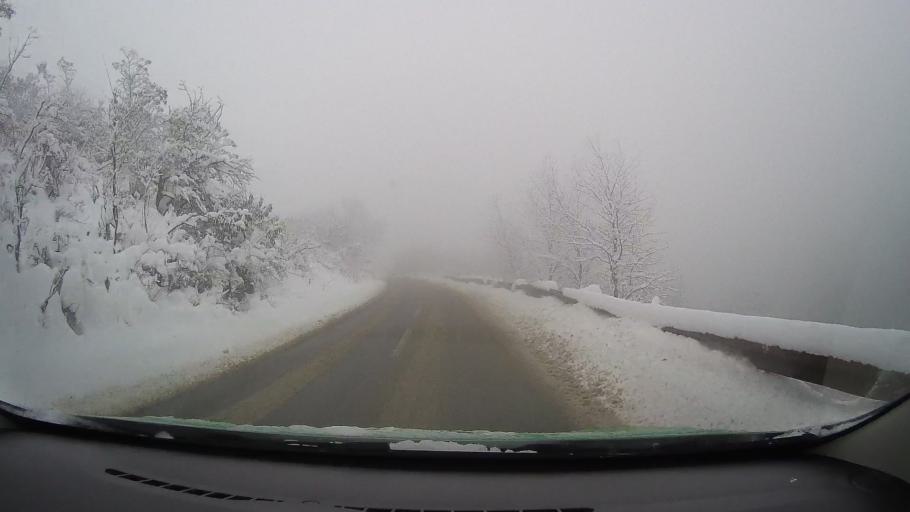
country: RO
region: Sibiu
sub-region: Comuna Poiana Sibiului
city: Poiana Sibiului
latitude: 45.7966
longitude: 23.7874
